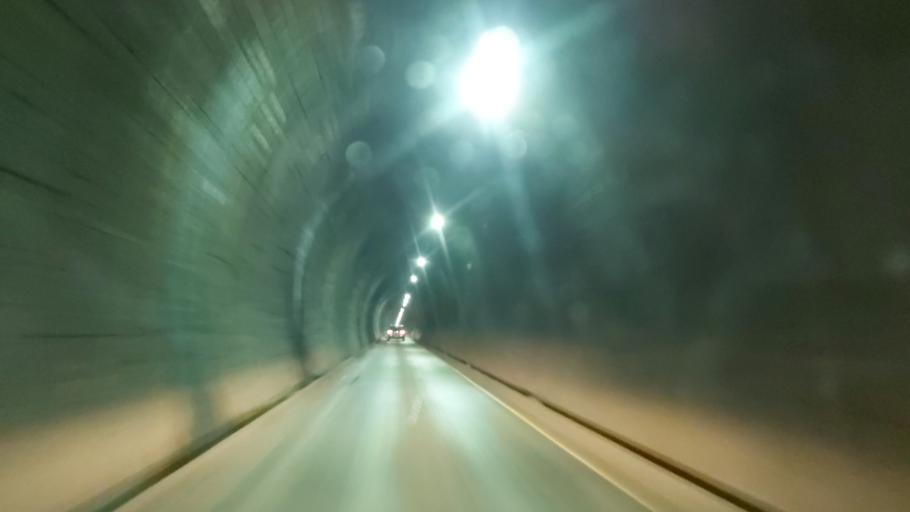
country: CL
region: Araucania
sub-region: Provincia de Cautin
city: Vilcun
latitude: -38.5363
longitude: -71.5081
